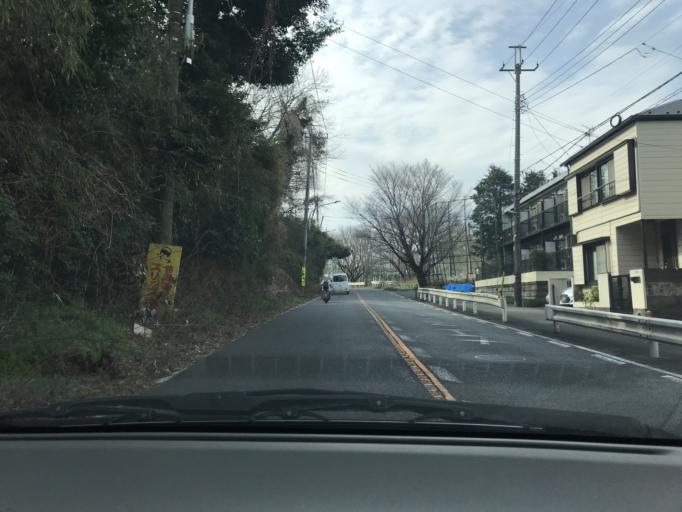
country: JP
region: Tokyo
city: Chofugaoka
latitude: 35.6127
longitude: 139.5521
